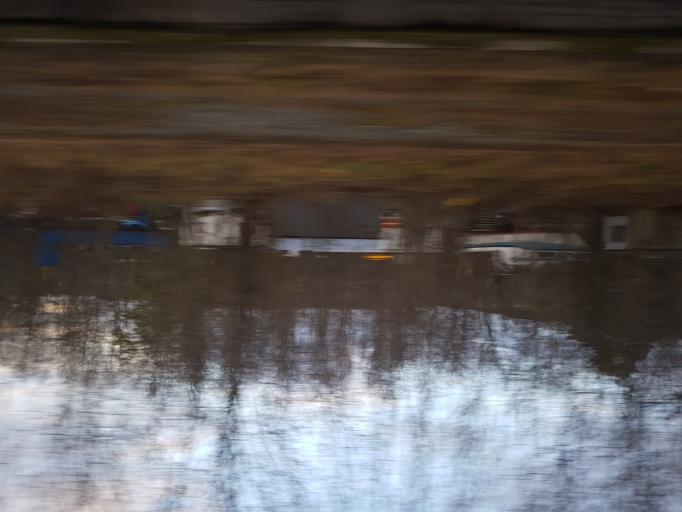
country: NO
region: Sor-Trondelag
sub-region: Melhus
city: Melhus
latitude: 63.2680
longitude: 10.2820
